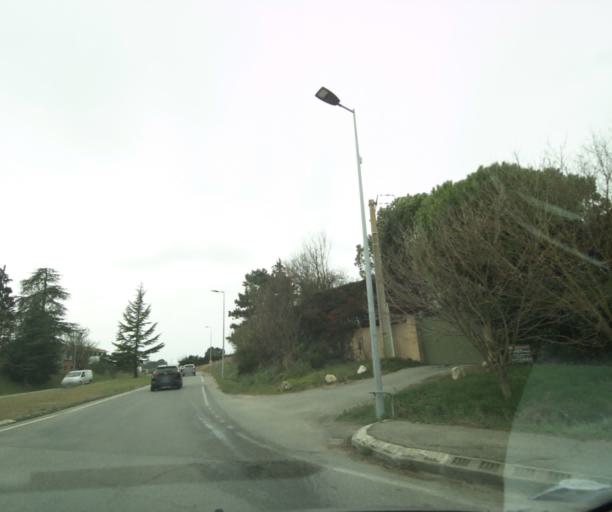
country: FR
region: Provence-Alpes-Cote d'Azur
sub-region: Departement des Bouches-du-Rhone
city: Aix-en-Provence
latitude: 43.5781
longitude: 5.4315
